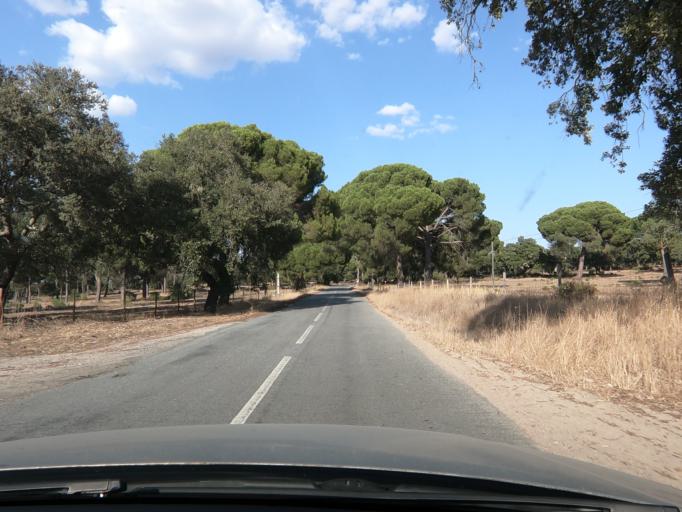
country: PT
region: Setubal
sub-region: Alcacer do Sal
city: Alcacer do Sal
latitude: 38.2613
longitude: -8.3531
